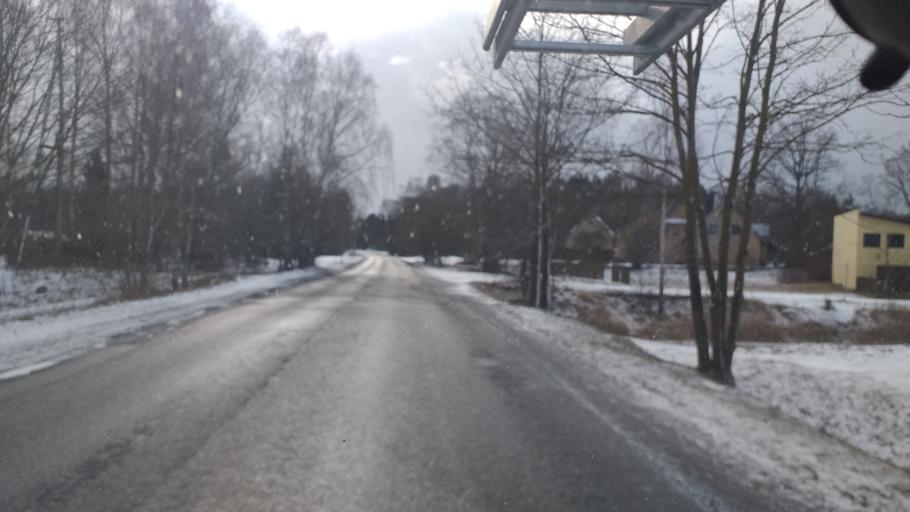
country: LV
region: Riga
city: Bolderaja
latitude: 56.9870
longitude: 24.0318
